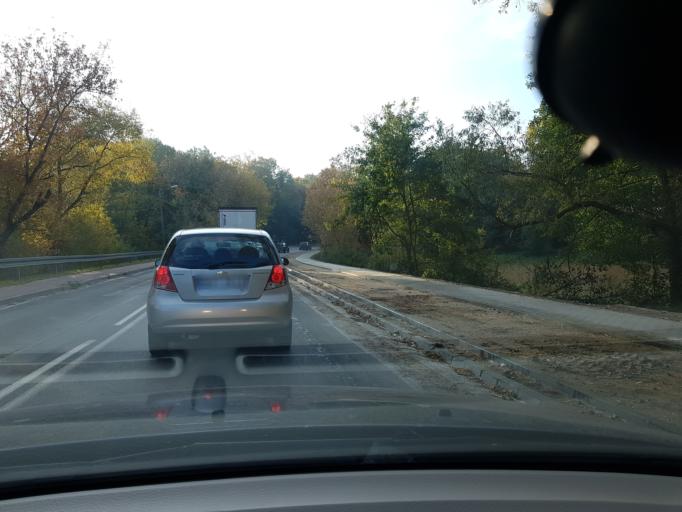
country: PL
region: Masovian Voivodeship
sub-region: Powiat otwocki
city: Jozefow
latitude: 52.1753
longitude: 21.2936
